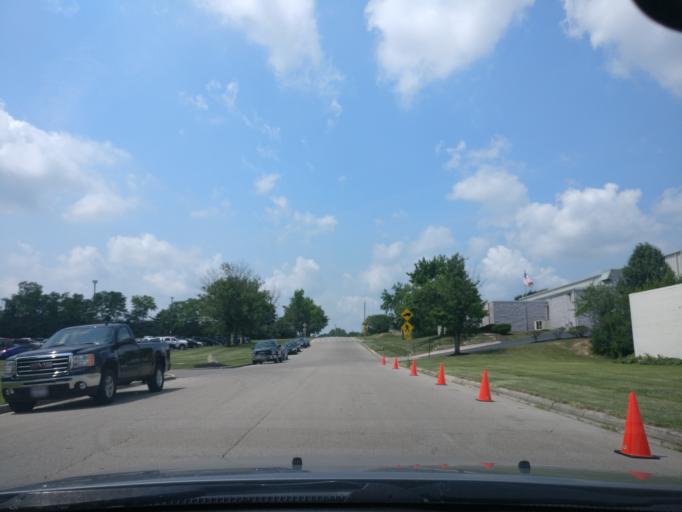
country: US
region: Ohio
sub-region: Montgomery County
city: West Carrollton City
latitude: 39.6550
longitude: -84.2386
